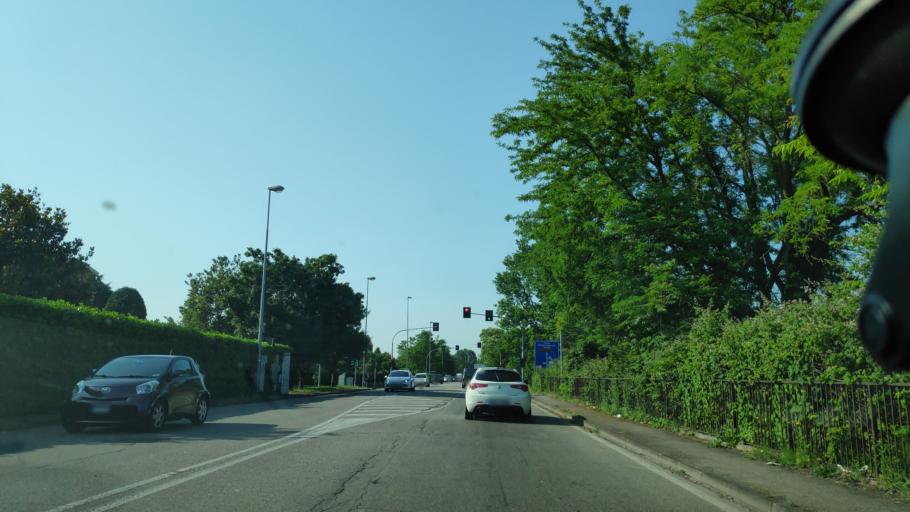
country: IT
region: Lombardy
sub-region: Citta metropolitana di Milano
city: Fizzonasco
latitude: 45.3681
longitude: 9.1893
